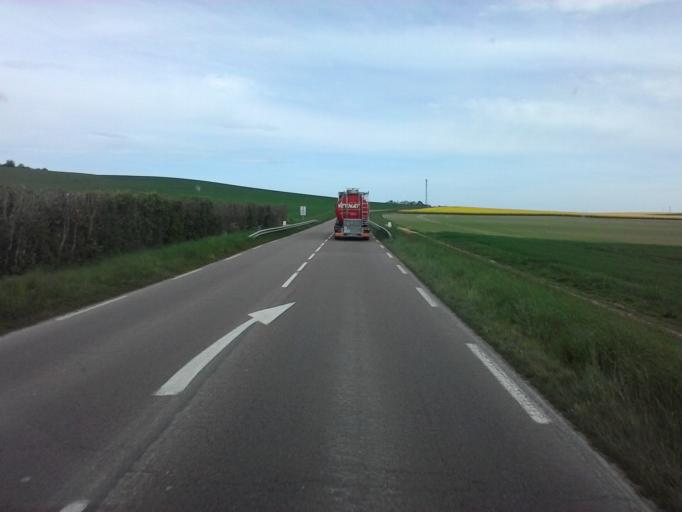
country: FR
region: Champagne-Ardenne
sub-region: Departement de l'Aube
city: Ervy-le-Chatel
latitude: 48.1102
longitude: 3.9224
